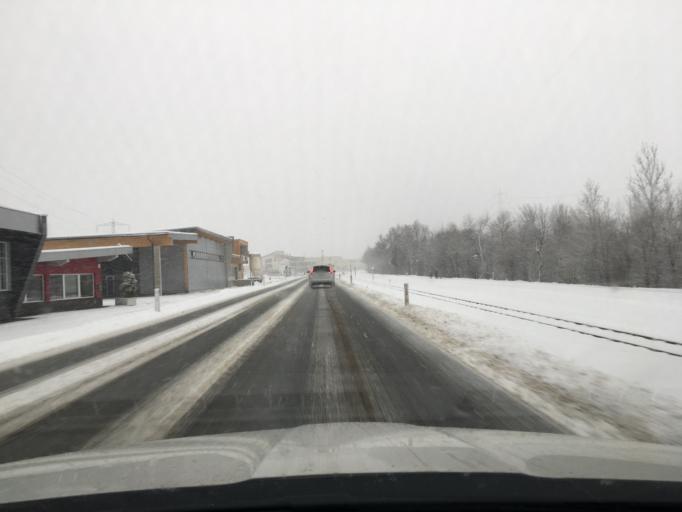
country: AT
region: Tyrol
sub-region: Politischer Bezirk Schwaz
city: Ramsau im Zillertal
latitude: 47.1968
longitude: 11.8713
